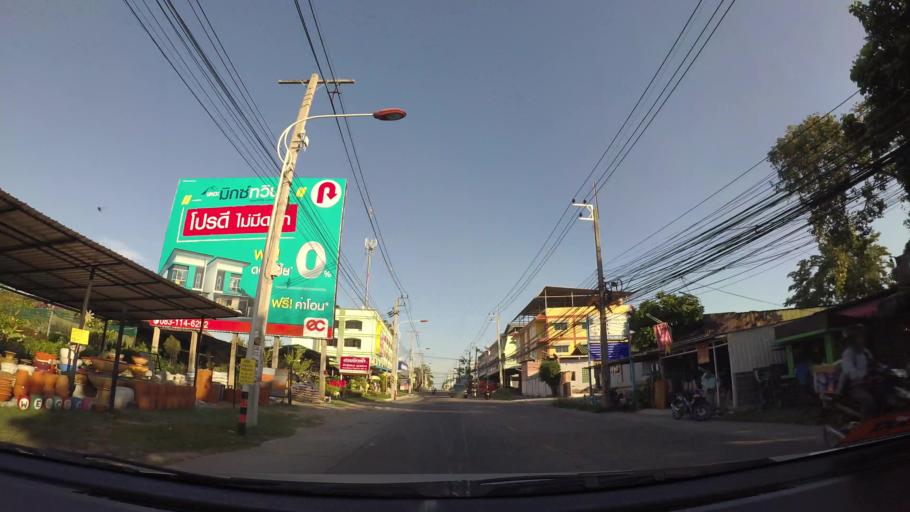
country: TH
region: Chon Buri
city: Si Racha
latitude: 13.1433
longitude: 100.9371
